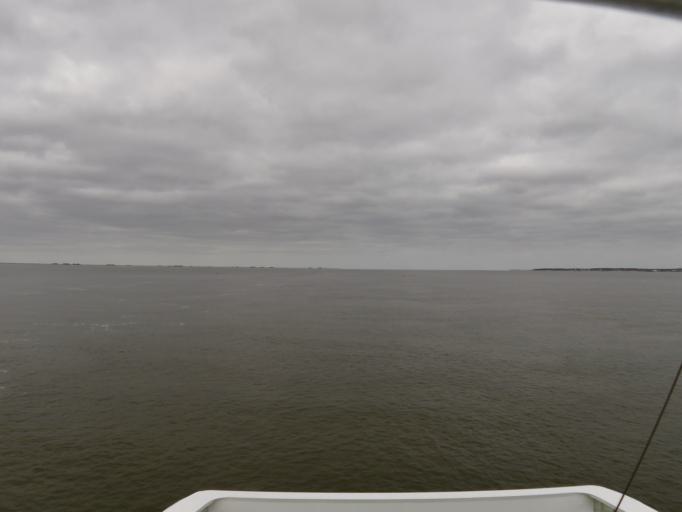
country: DE
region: Schleswig-Holstein
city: Dagebull
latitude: 54.7018
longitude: 8.6402
